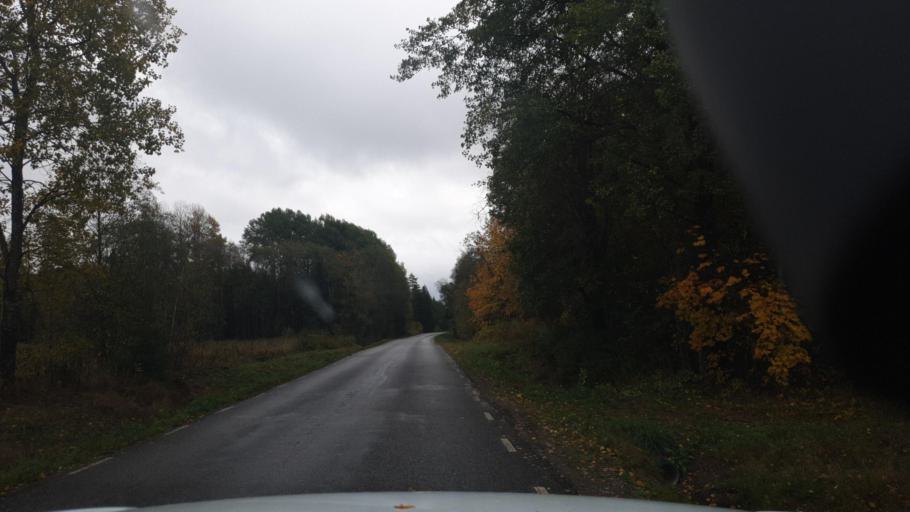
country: SE
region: Vaermland
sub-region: Karlstads Kommun
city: Valberg
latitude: 59.4133
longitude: 13.1658
